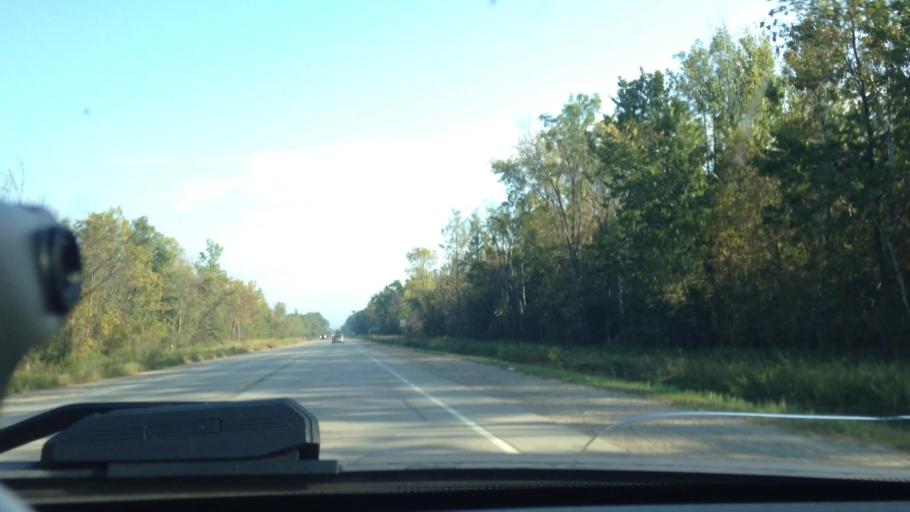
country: US
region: Wisconsin
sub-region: Marinette County
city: Peshtigo
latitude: 45.2374
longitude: -87.9958
